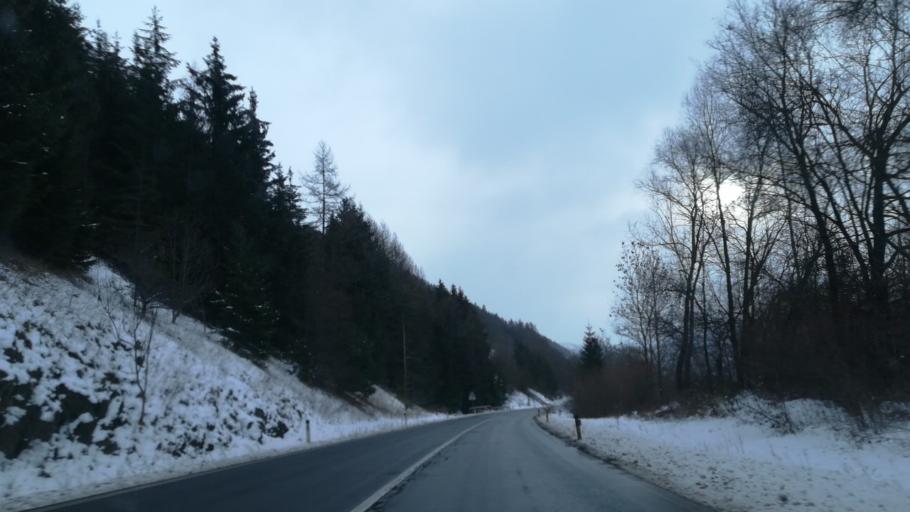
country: AT
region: Styria
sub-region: Politischer Bezirk Murtal
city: Poels
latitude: 47.2075
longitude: 14.5810
